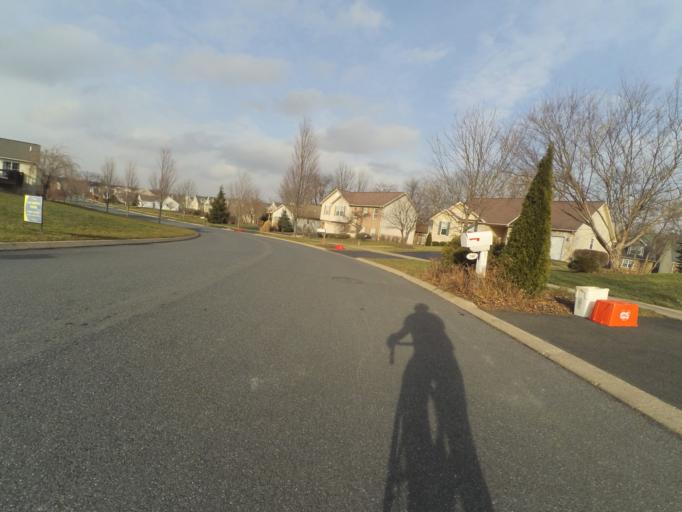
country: US
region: Pennsylvania
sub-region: Centre County
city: Park Forest Village
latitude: 40.7849
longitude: -77.8963
